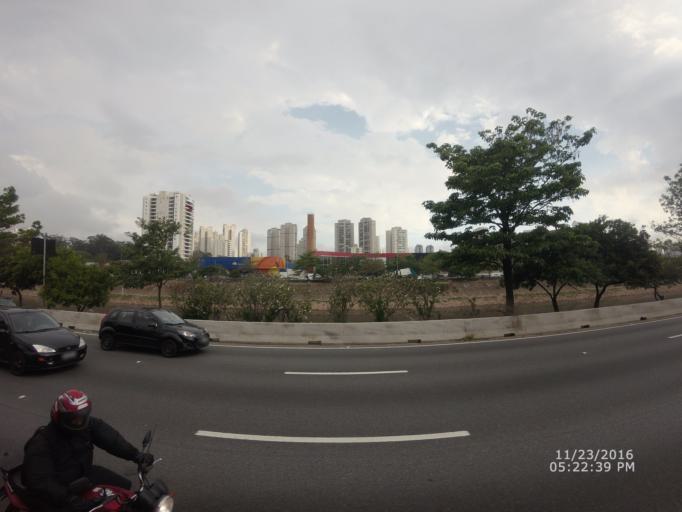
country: BR
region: Sao Paulo
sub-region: Sao Paulo
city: Sao Paulo
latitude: -23.5263
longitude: -46.5787
